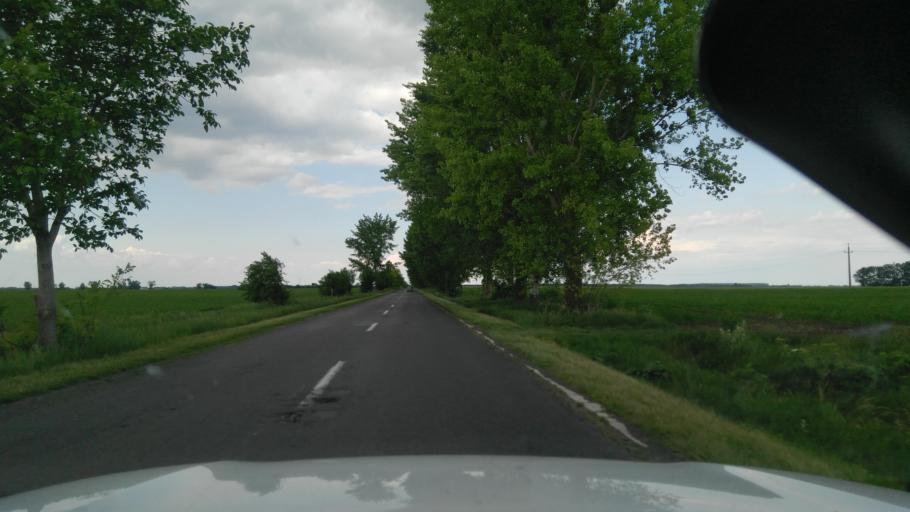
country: HU
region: Bekes
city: Magyarbanhegyes
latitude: 46.4540
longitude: 20.9984
